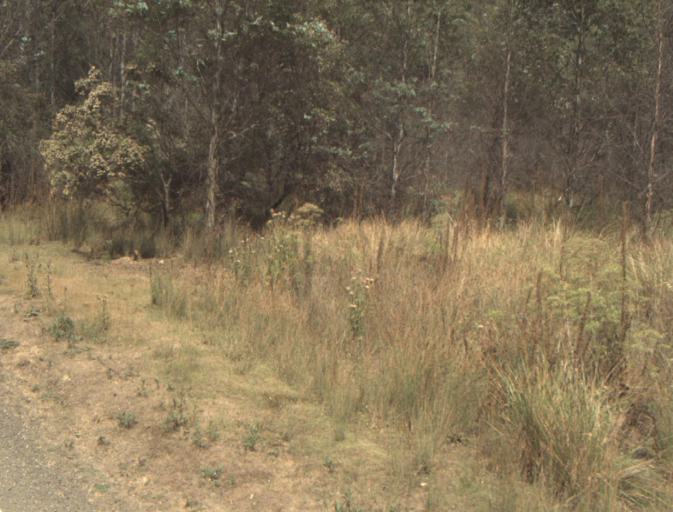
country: AU
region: Tasmania
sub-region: Launceston
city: Mayfield
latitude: -41.1968
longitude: 147.2627
